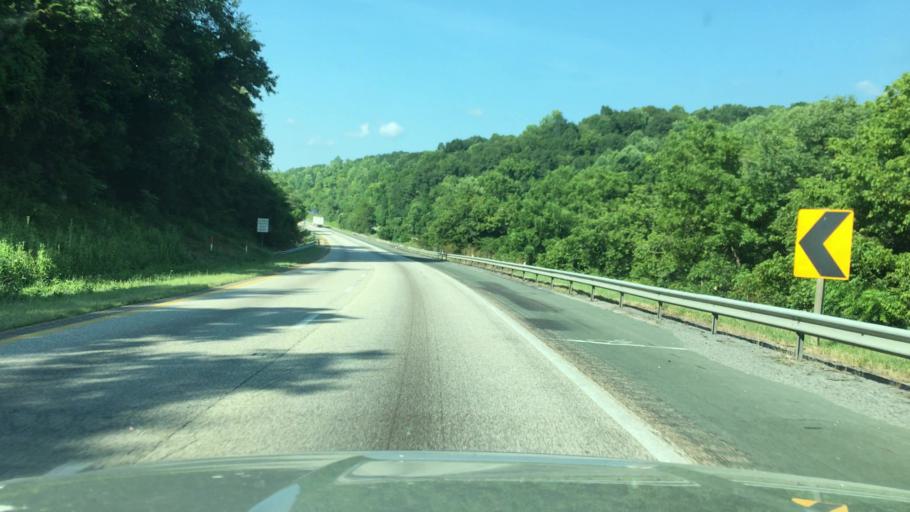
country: US
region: Virginia
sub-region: Botetourt County
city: Buchanan
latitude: 37.6128
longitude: -79.5922
